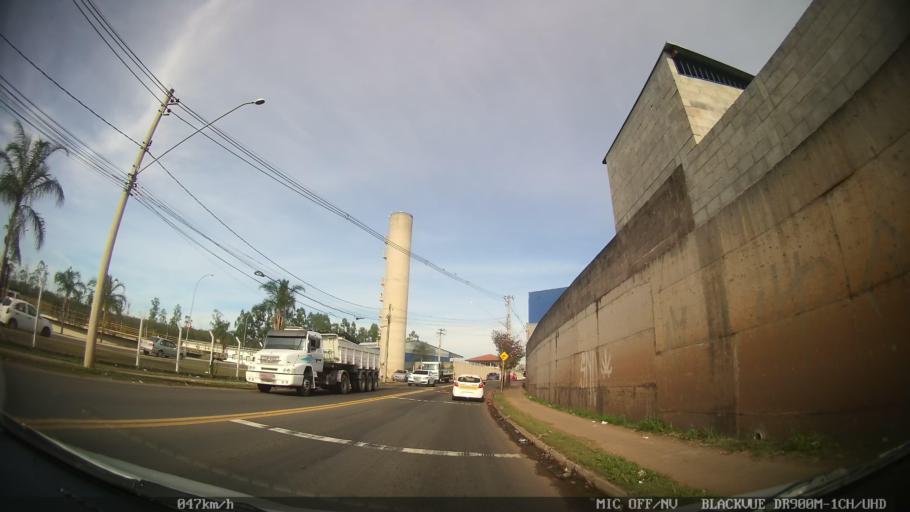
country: BR
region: Sao Paulo
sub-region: Piracicaba
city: Piracicaba
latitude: -22.6996
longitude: -47.6745
